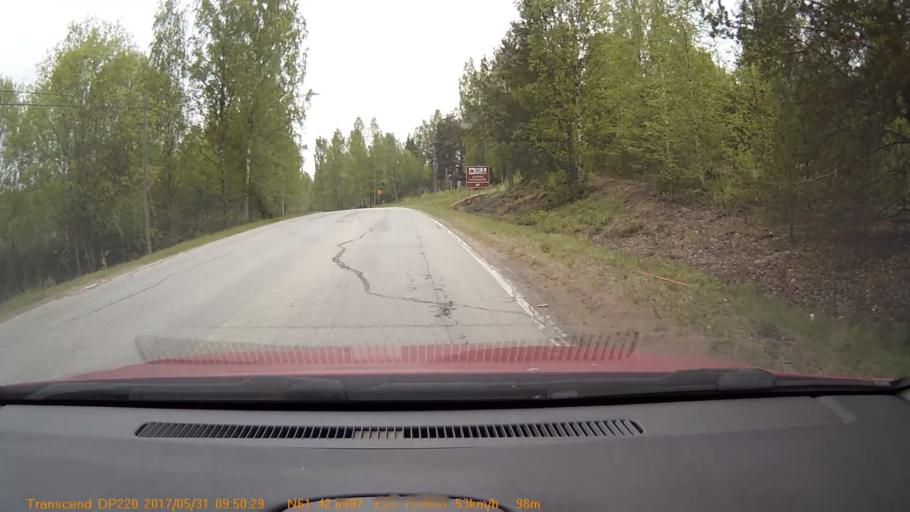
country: FI
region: Pirkanmaa
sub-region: Tampere
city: Viljakkala
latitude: 61.7118
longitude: 23.2502
